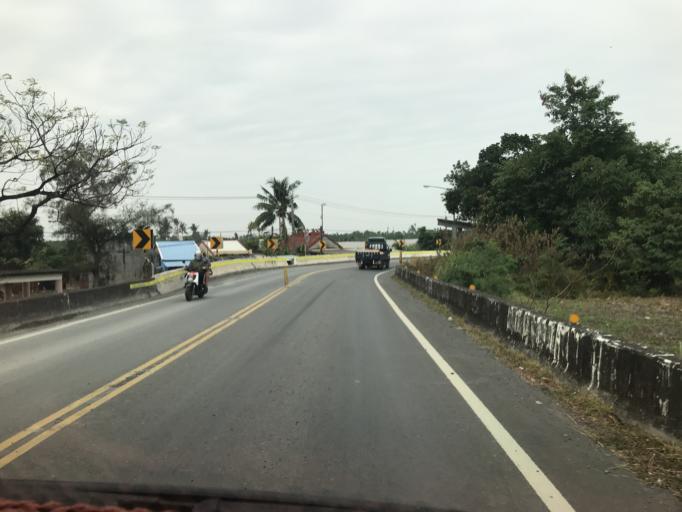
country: TW
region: Taiwan
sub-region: Pingtung
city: Pingtung
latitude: 22.4953
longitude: 120.5910
